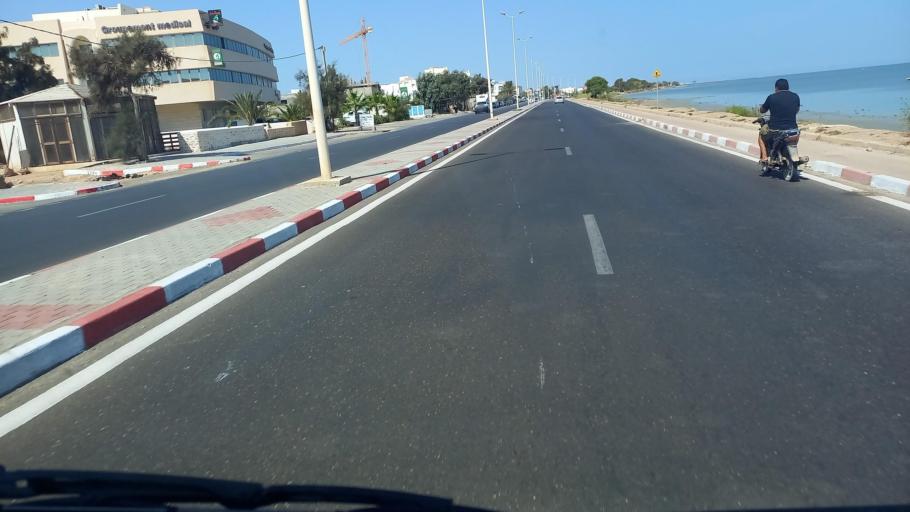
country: TN
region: Madanin
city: Houmt Souk
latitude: 33.8745
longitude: 10.8951
